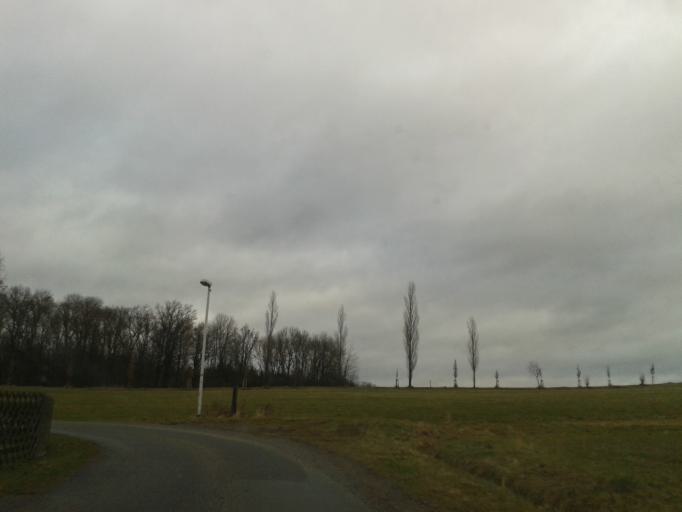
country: DE
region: Saxony
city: Neugersdorf
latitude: 50.9619
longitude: 14.6216
